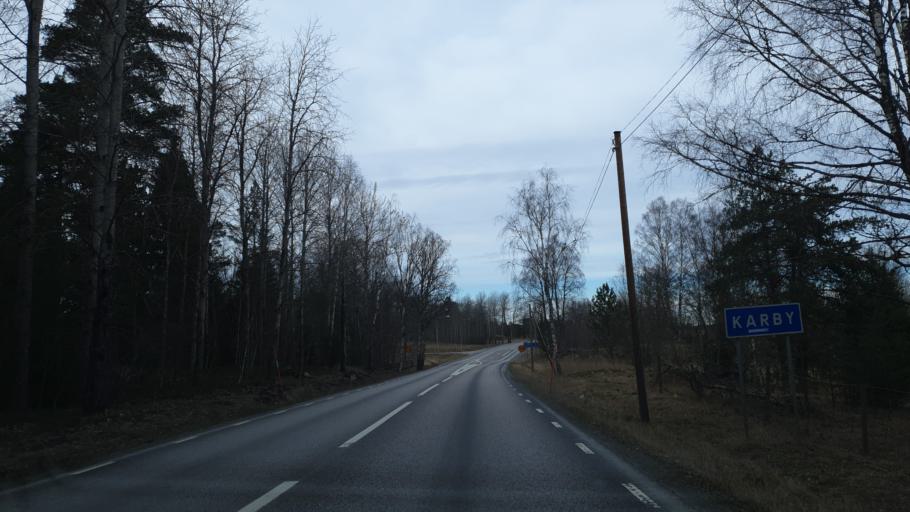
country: SE
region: Stockholm
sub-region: Osterakers Kommun
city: Akersberga
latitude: 59.5554
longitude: 18.2200
